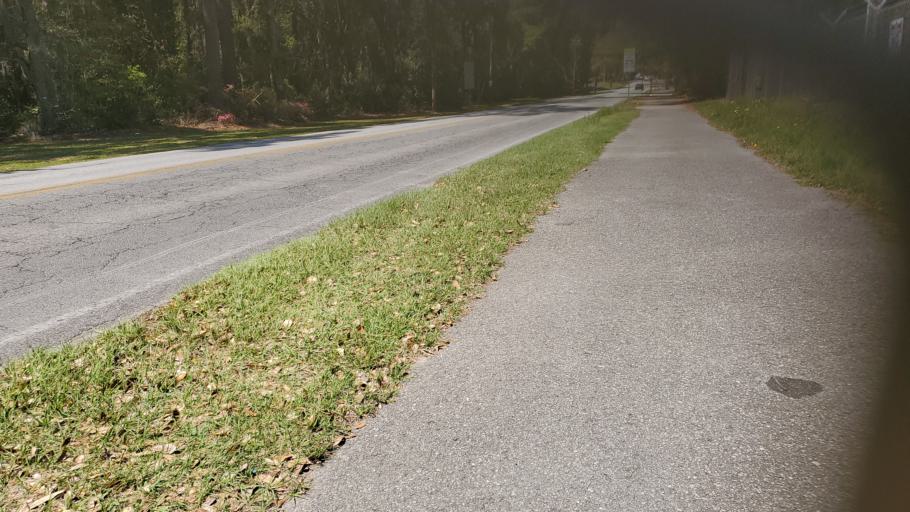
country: US
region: Georgia
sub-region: Chatham County
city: Wilmington Island
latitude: 32.0038
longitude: -80.9864
